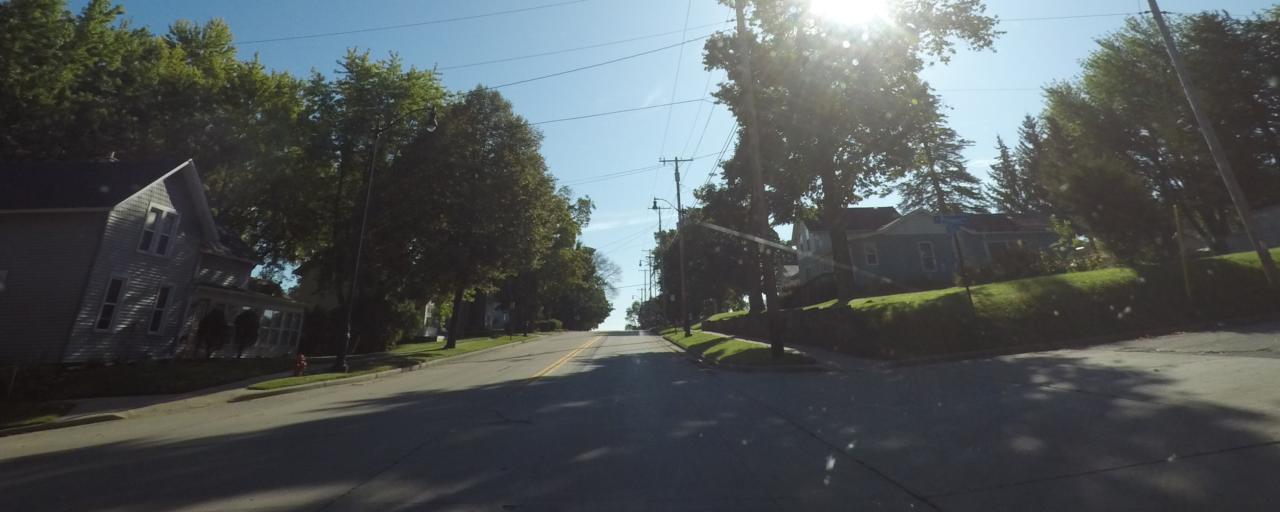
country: US
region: Wisconsin
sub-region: Jefferson County
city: Jefferson
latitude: 43.0055
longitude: -88.8144
